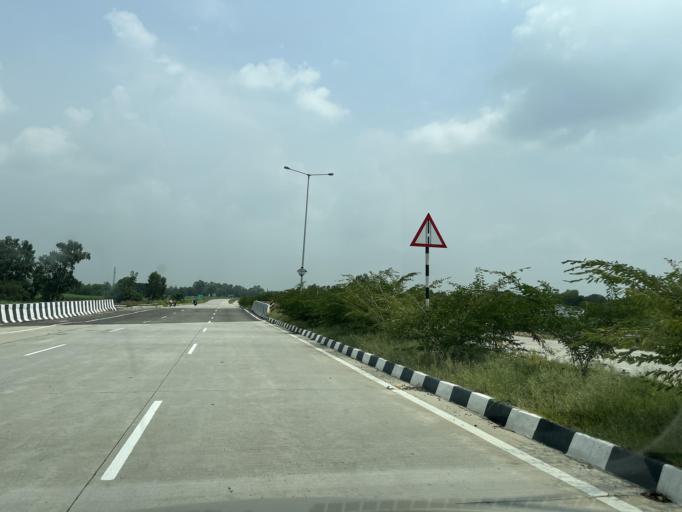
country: IN
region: Uttar Pradesh
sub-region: Bijnor
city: Nagina
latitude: 29.4252
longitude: 78.4364
